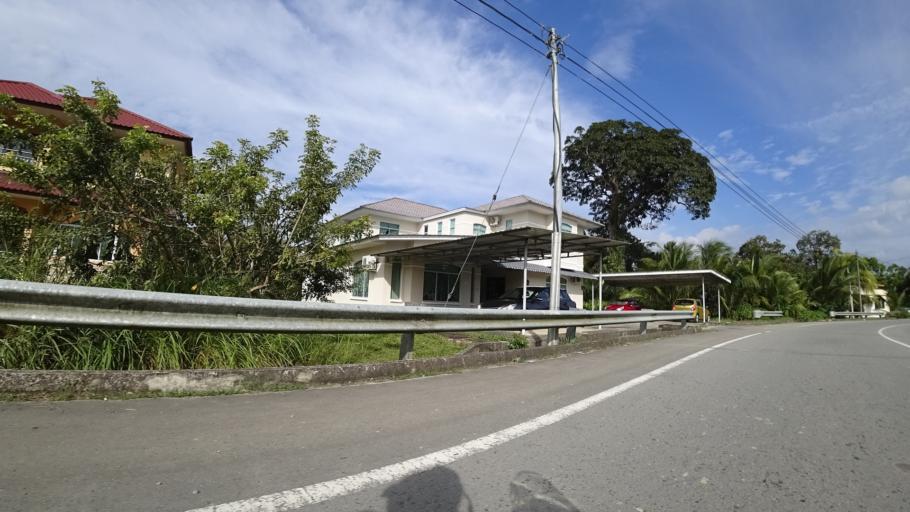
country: BN
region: Brunei and Muara
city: Bandar Seri Begawan
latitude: 4.8730
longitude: 114.8073
